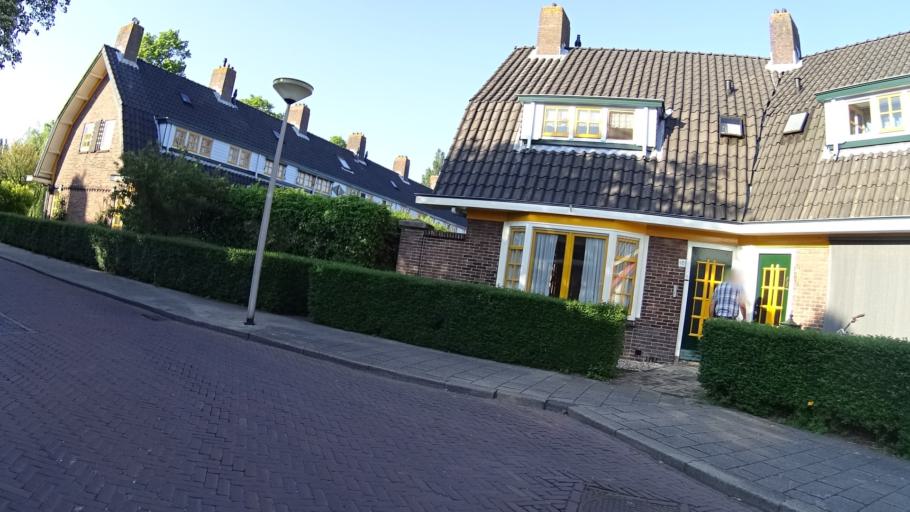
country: NL
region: South Holland
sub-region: Gemeente Delft
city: Delft
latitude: 52.0147
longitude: 4.3438
